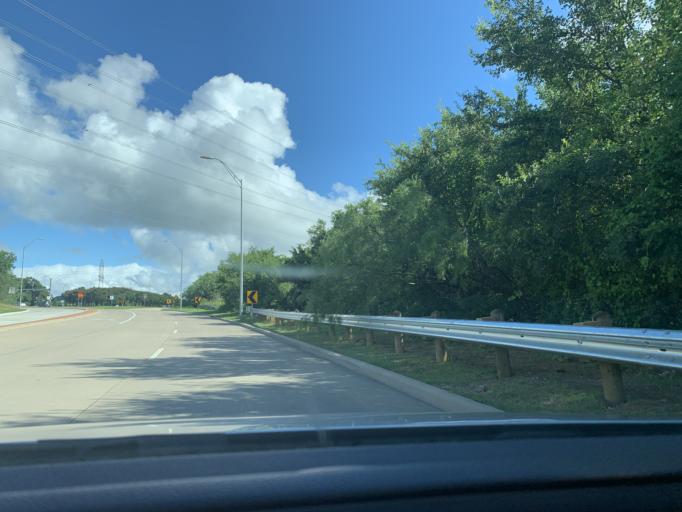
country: US
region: Texas
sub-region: Dallas County
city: Grand Prairie
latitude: 32.6577
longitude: -97.0421
